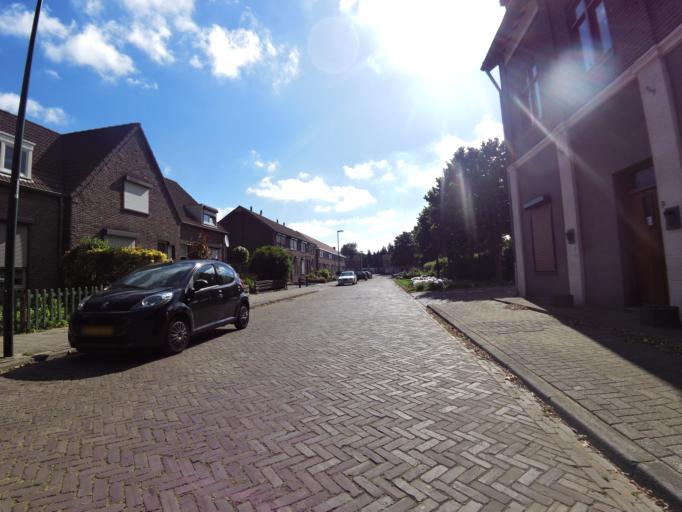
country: NL
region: Limburg
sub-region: Gemeente Brunssum
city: Brunssum
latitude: 50.9217
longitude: 5.9743
